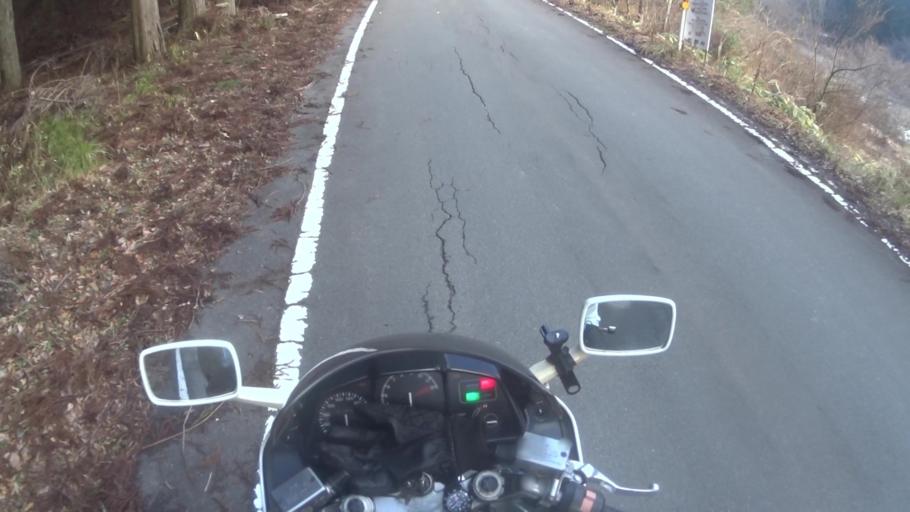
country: JP
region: Kyoto
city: Maizuru
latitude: 35.3868
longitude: 135.4709
